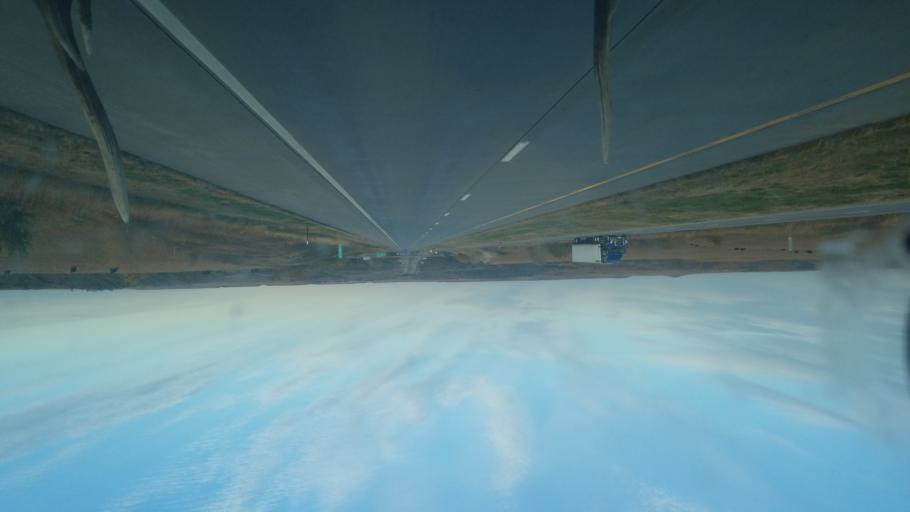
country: US
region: Kansas
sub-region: Riley County
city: Ogden
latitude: 39.0660
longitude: -96.6685
